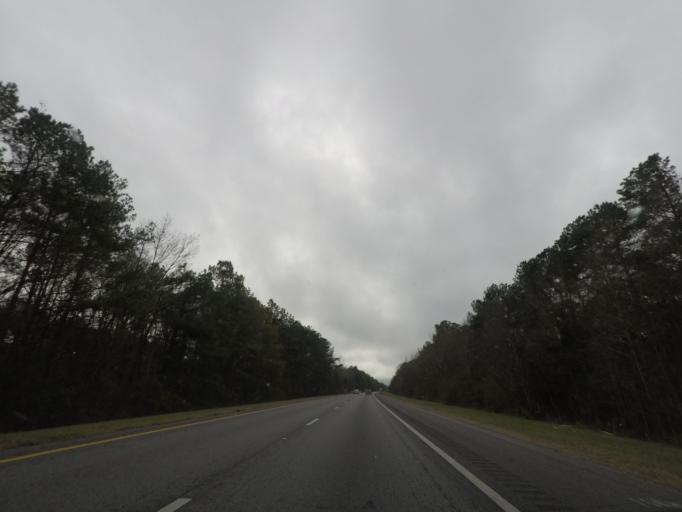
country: US
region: South Carolina
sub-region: Orangeburg County
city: Holly Hill
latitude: 33.3566
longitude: -80.5285
